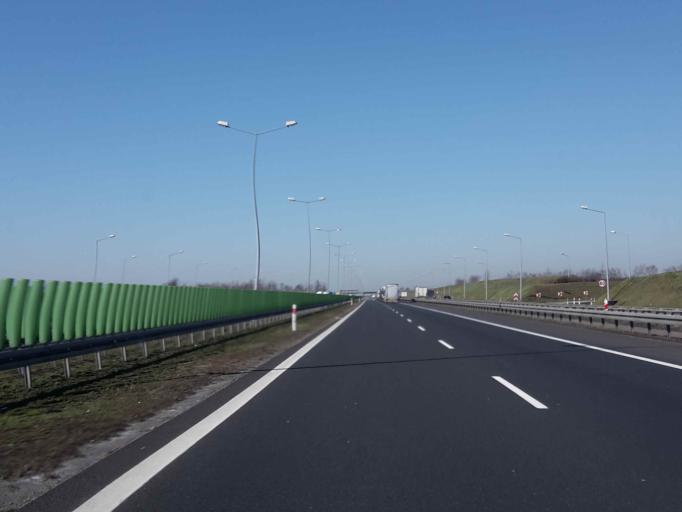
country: PL
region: Greater Poland Voivodeship
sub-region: Powiat poznanski
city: Daszewice
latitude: 52.3461
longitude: 16.9983
